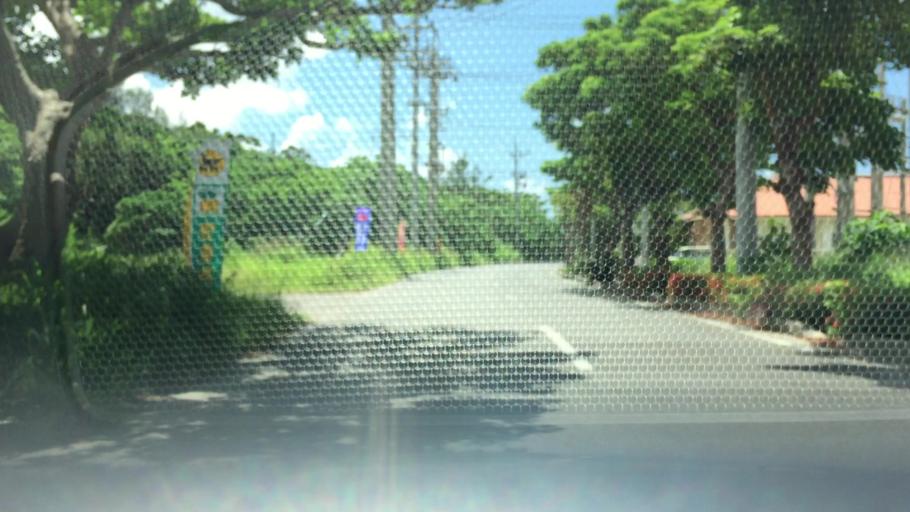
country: JP
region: Okinawa
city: Ishigaki
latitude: 24.3638
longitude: 124.1158
